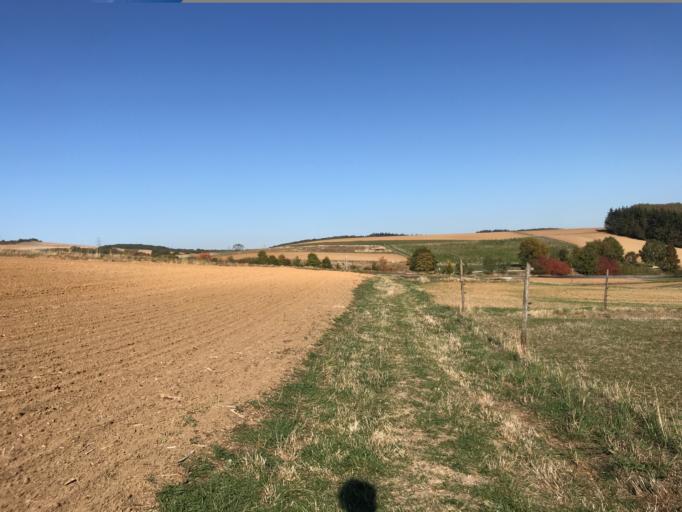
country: DE
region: Rheinland-Pfalz
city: Lonnig
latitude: 50.3126
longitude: 7.4330
